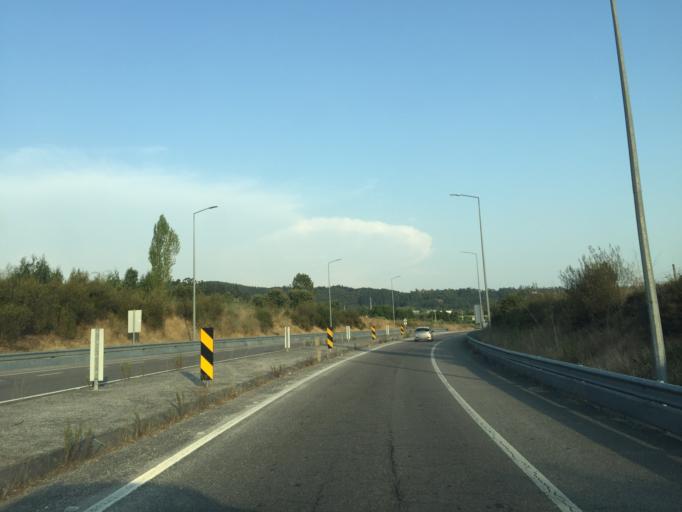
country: PT
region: Santarem
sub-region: Tomar
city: Tomar
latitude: 39.5942
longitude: -8.3623
